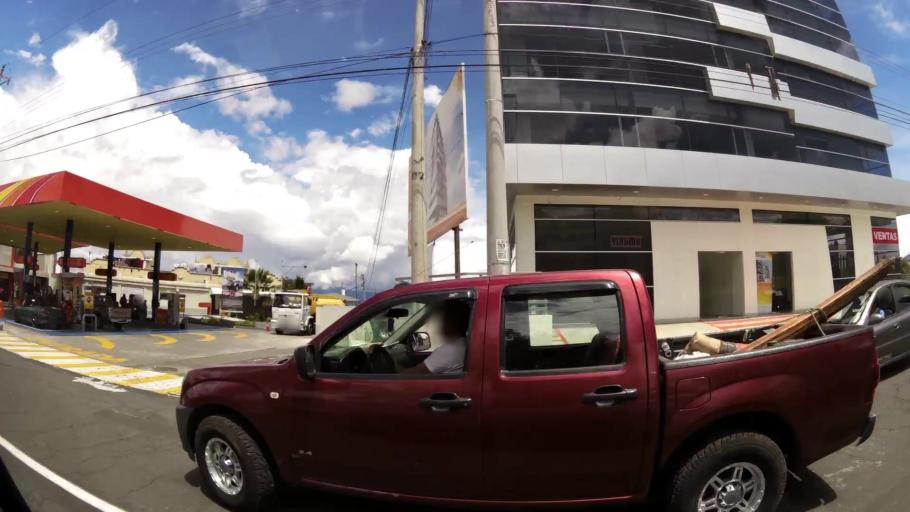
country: EC
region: Tungurahua
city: Ambato
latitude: -1.2690
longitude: -78.6377
